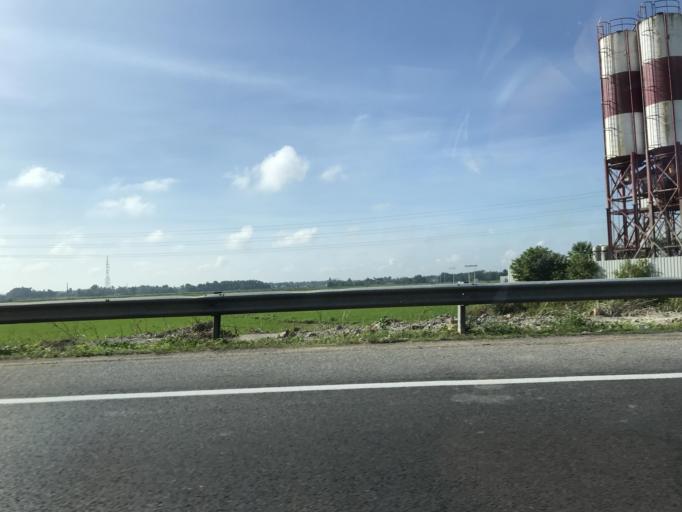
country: MY
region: Kelantan
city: Kampong Kadok
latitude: 6.0529
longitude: 102.2253
